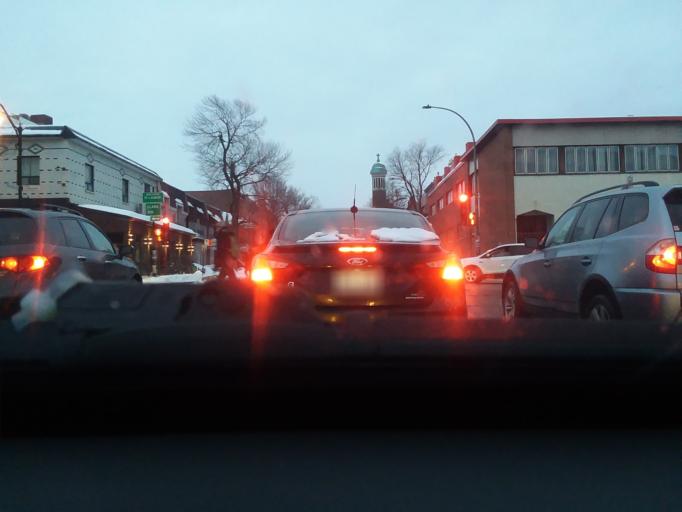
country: CA
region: Quebec
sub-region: Montreal
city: Montreal
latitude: 45.5262
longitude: -73.6035
